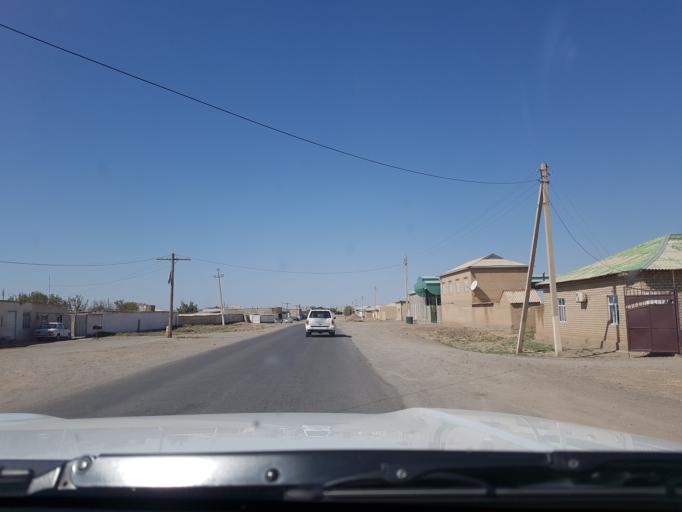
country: IR
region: Razavi Khorasan
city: Sarakhs
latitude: 36.5135
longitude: 61.2226
